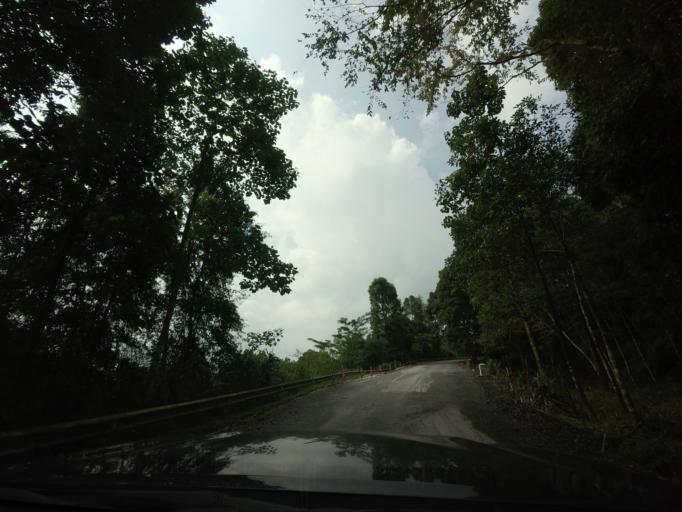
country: TH
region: Nan
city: Bo Kluea
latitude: 19.2064
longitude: 101.0715
